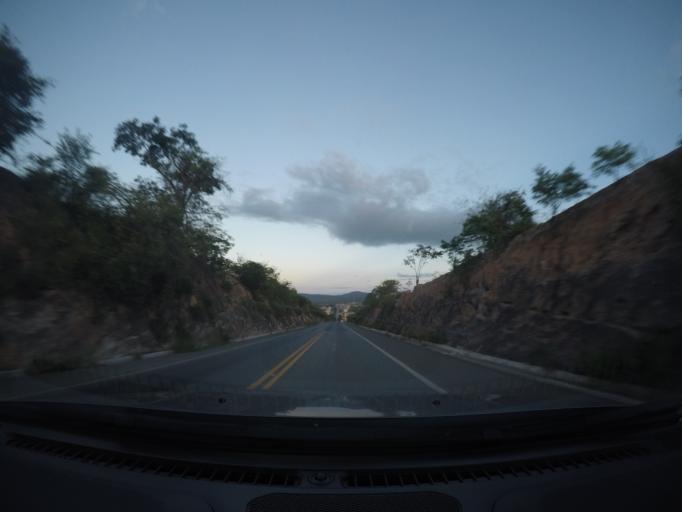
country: BR
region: Bahia
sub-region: Seabra
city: Seabra
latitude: -12.4293
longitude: -41.7863
